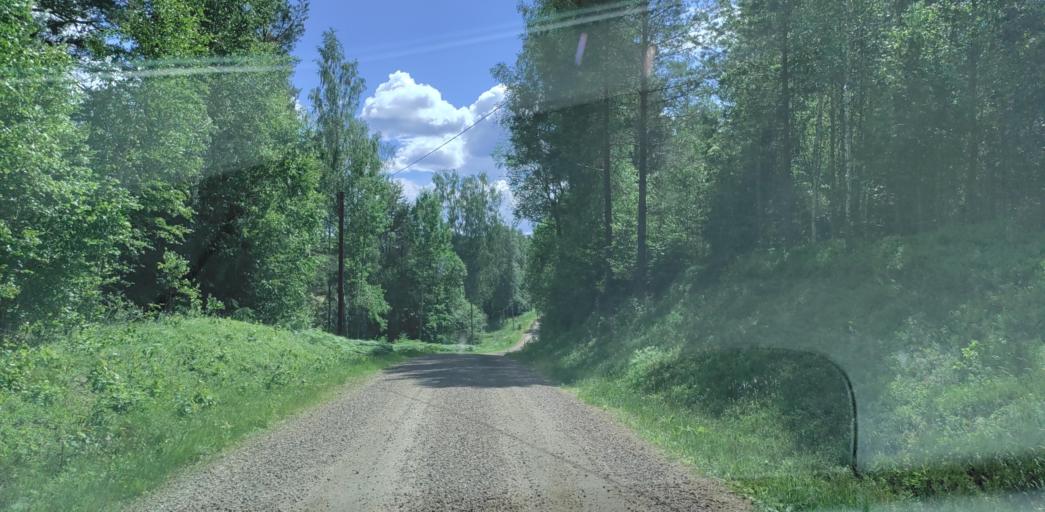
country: SE
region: Vaermland
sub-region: Munkfors Kommun
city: Munkfors
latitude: 59.9666
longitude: 13.5219
